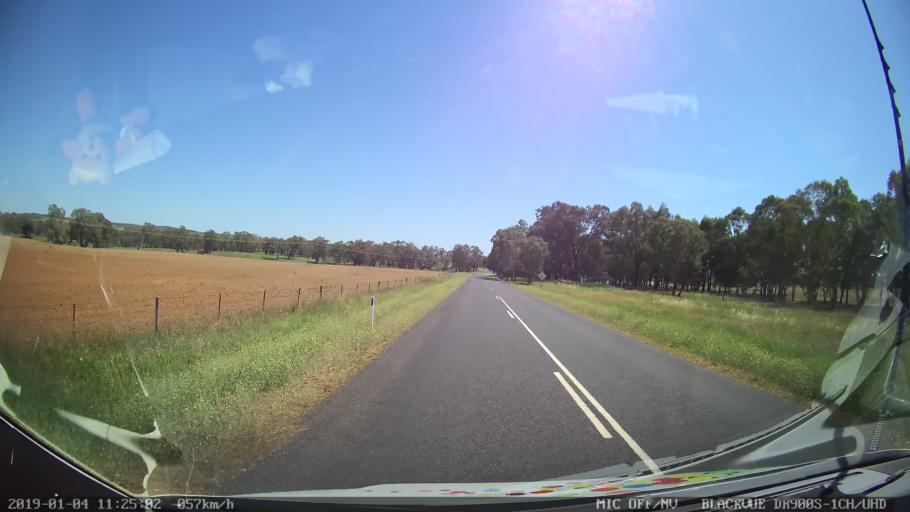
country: AU
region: New South Wales
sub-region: Cabonne
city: Molong
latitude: -33.1293
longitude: 148.7523
